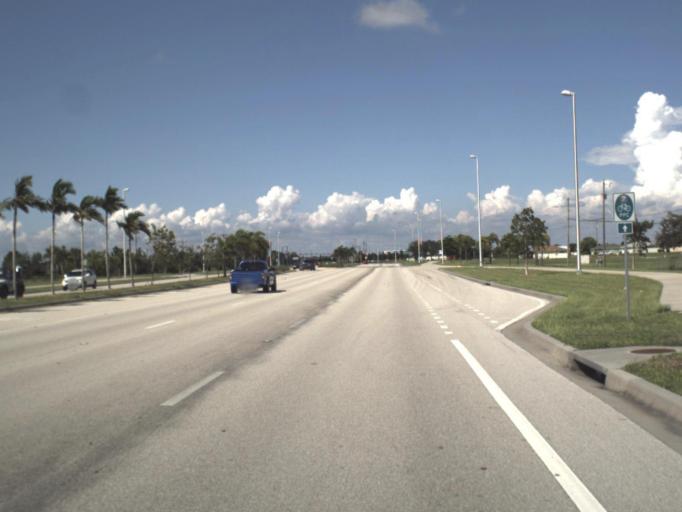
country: US
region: Florida
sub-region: Lee County
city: Lochmoor Waterway Estates
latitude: 26.6770
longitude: -81.9414
